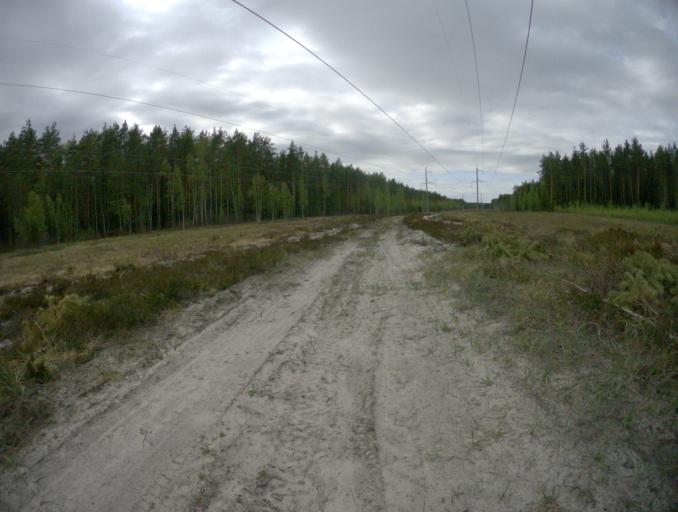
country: RU
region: Vladimir
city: Golovino
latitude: 55.9242
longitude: 40.4792
